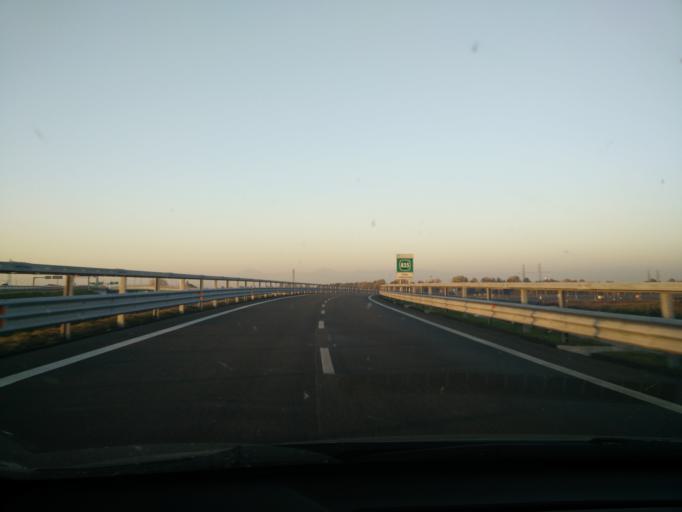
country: IT
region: Lombardy
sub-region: Citta metropolitana di Milano
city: Pozzuolo Martesana
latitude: 45.5011
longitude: 9.4449
